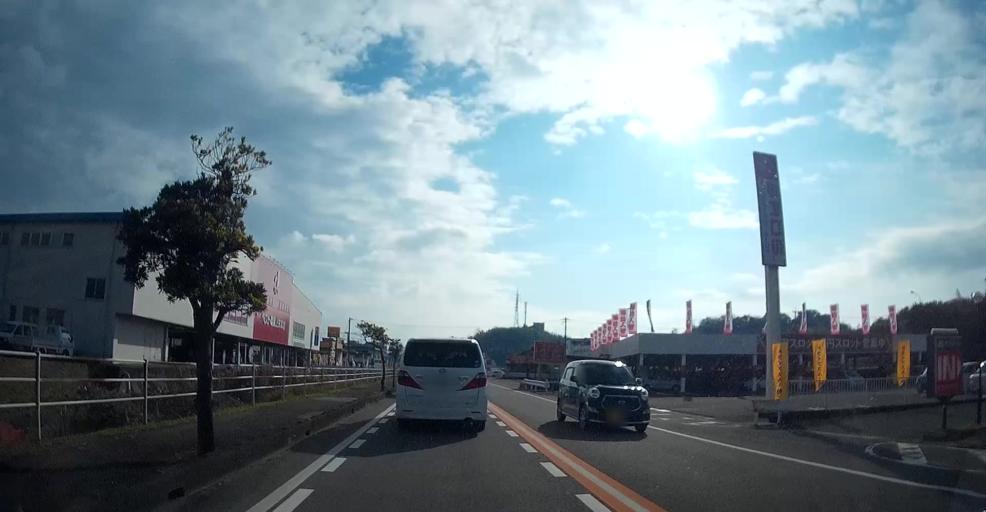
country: JP
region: Kumamoto
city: Yatsushiro
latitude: 32.5911
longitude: 130.4299
